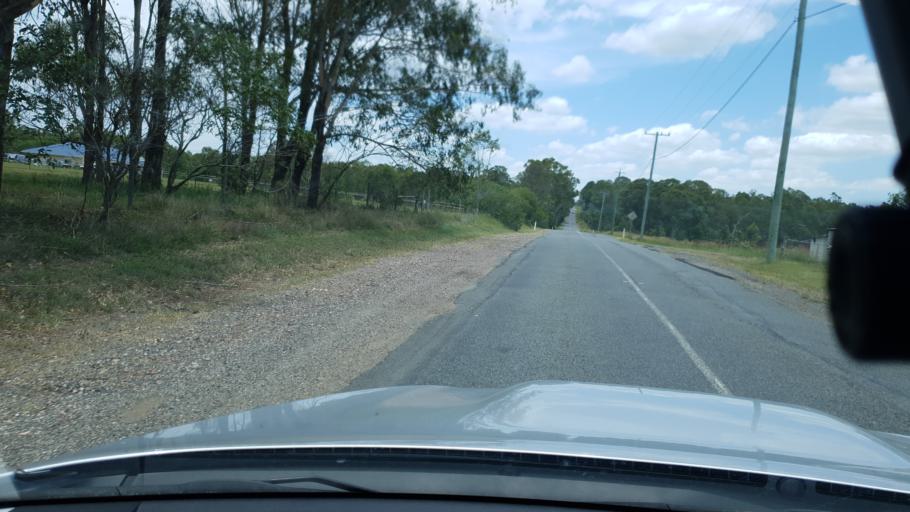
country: AU
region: Queensland
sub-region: Logan
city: North Maclean
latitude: -27.7732
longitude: 152.9987
